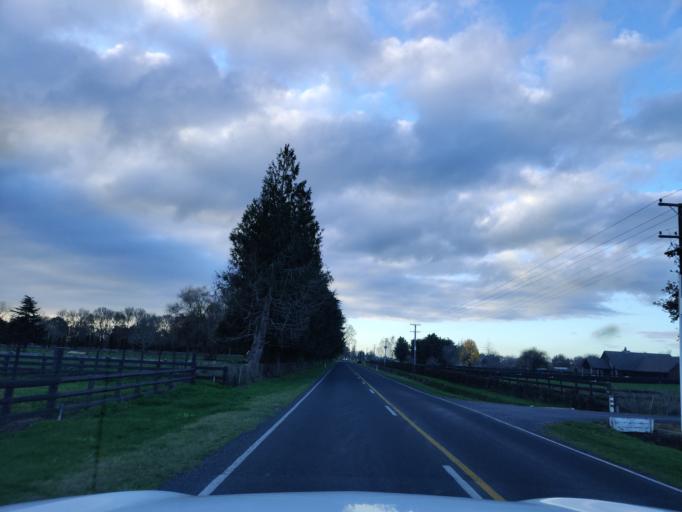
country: NZ
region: Waikato
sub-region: Waipa District
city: Cambridge
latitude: -37.8516
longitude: 175.4390
